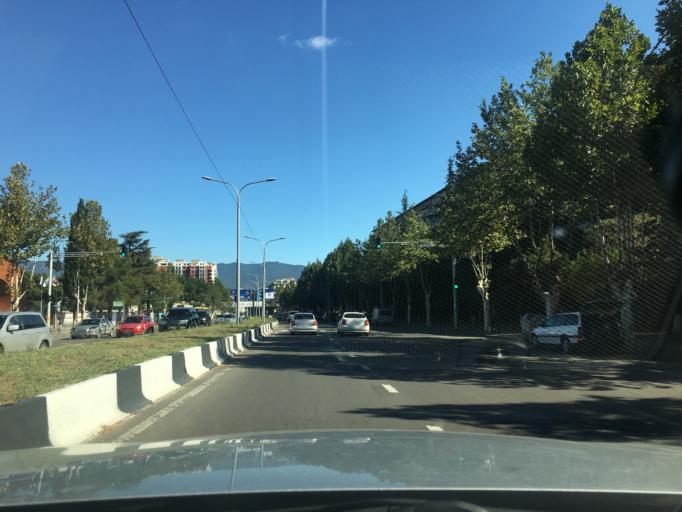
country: GE
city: Zahesi
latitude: 41.7675
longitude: 44.7914
